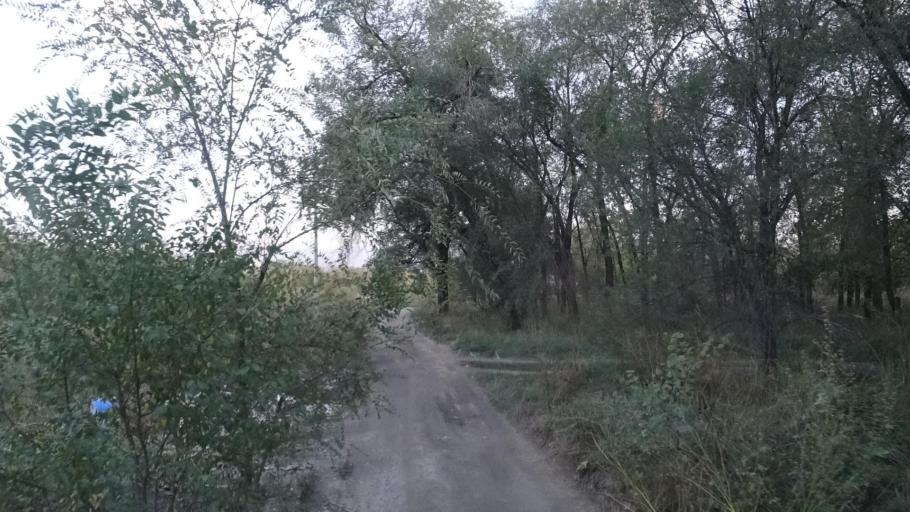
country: KZ
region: Almaty Oblysy
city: Pervomayskiy
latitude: 43.3360
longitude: 76.9987
